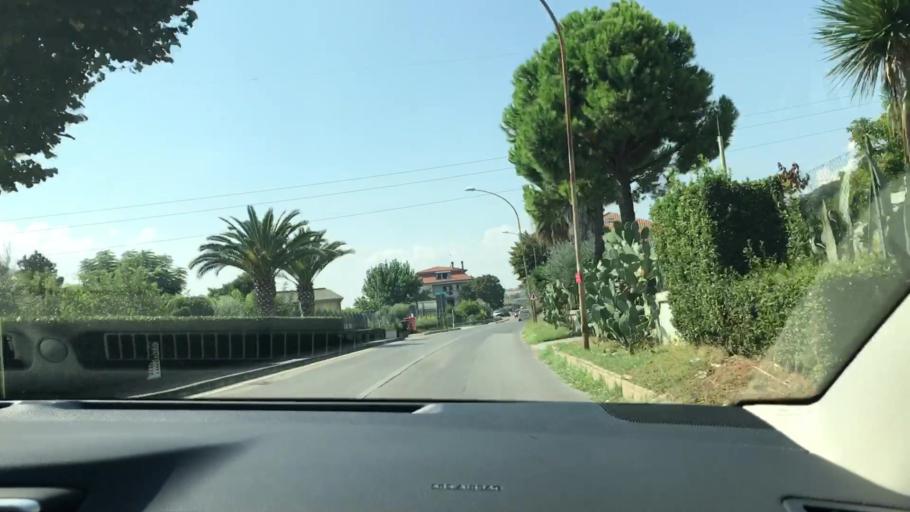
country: IT
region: The Marches
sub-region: Provincia di Ascoli Piceno
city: San Benedetto del Tronto
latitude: 42.9066
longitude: 13.8716
